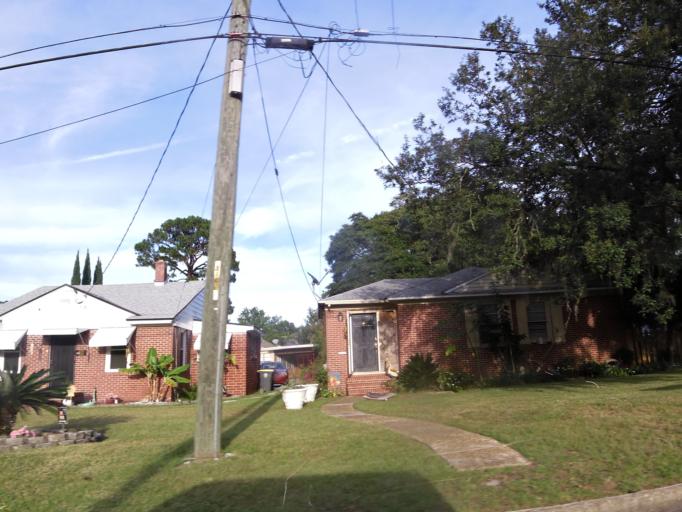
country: US
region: Florida
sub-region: Duval County
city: Jacksonville
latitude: 30.3864
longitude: -81.6624
